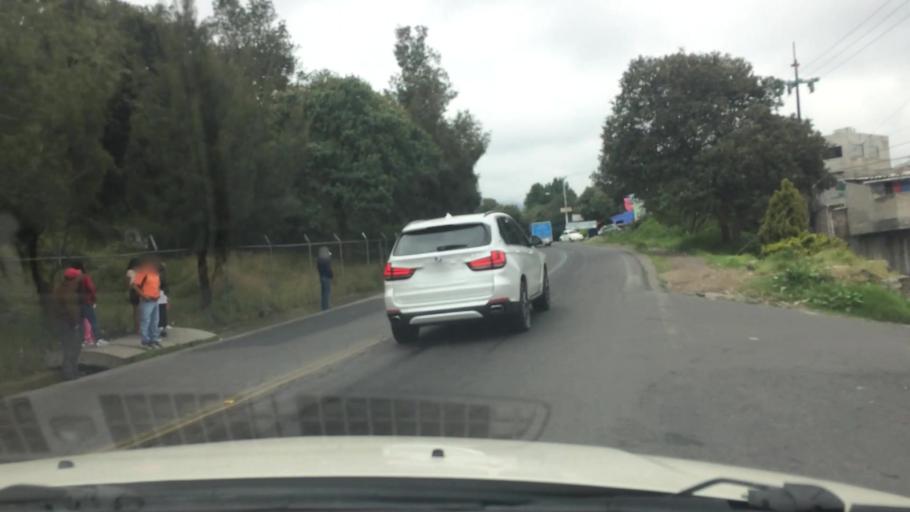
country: MX
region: Mexico City
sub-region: Tlalpan
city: Lomas de Tepemecatl
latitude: 19.2681
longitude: -99.2221
